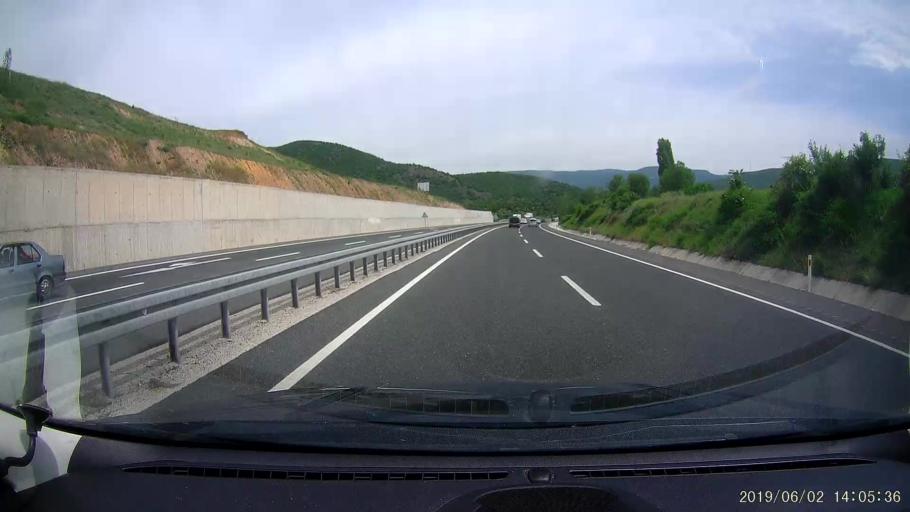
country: TR
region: Cankiri
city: Ilgaz
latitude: 40.8998
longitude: 33.6716
